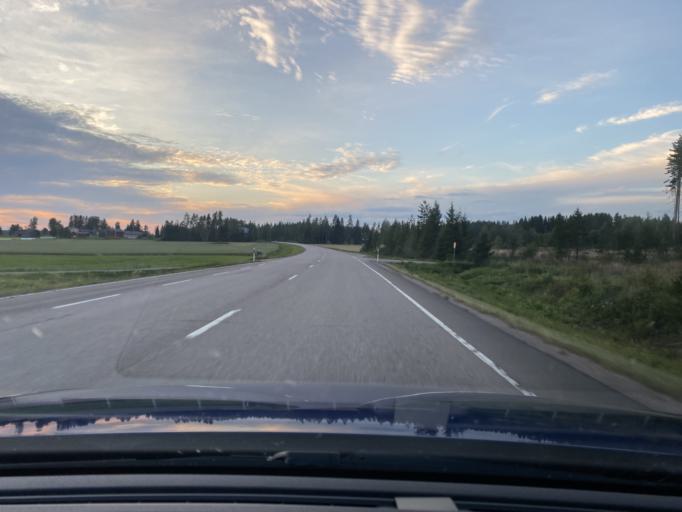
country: FI
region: Satakunta
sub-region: Pohjois-Satakunta
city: Kankaanpaeae
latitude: 61.8637
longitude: 22.3176
